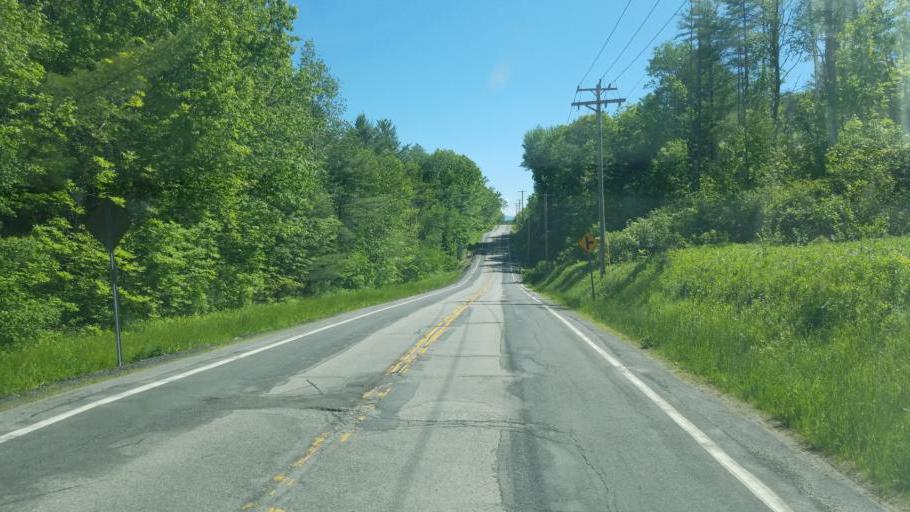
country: US
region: New York
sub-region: Montgomery County
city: Canajoharie
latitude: 43.0382
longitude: -74.5295
